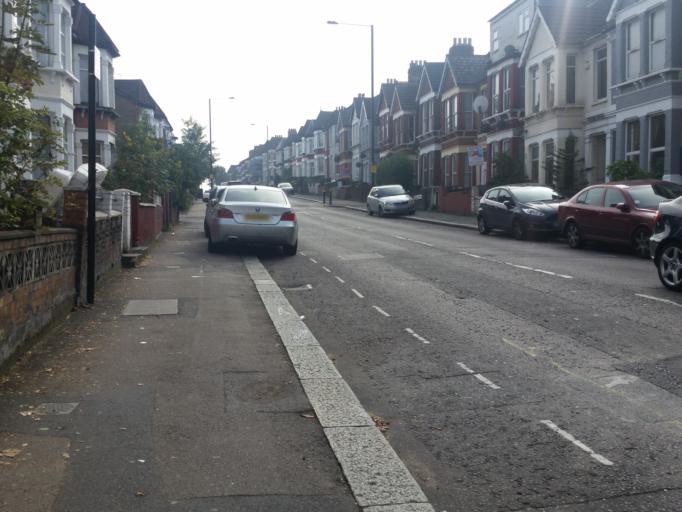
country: GB
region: England
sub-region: Greater London
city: Harringay
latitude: 51.5807
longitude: -0.1056
